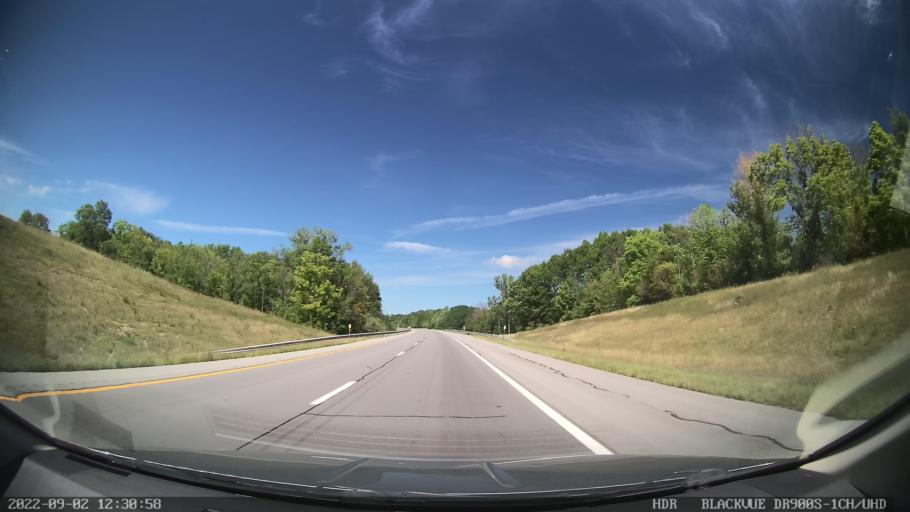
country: US
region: New York
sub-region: Livingston County
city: Dansville
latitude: 42.6019
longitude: -77.7527
